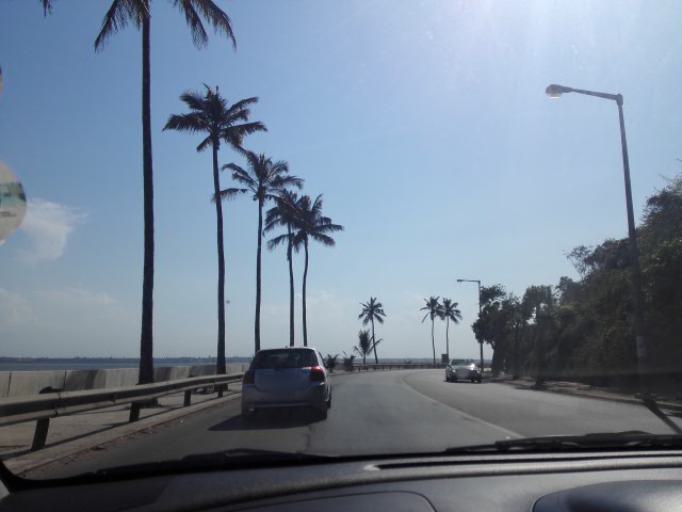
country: MZ
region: Maputo City
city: Maputo
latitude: -25.9835
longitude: 32.5935
